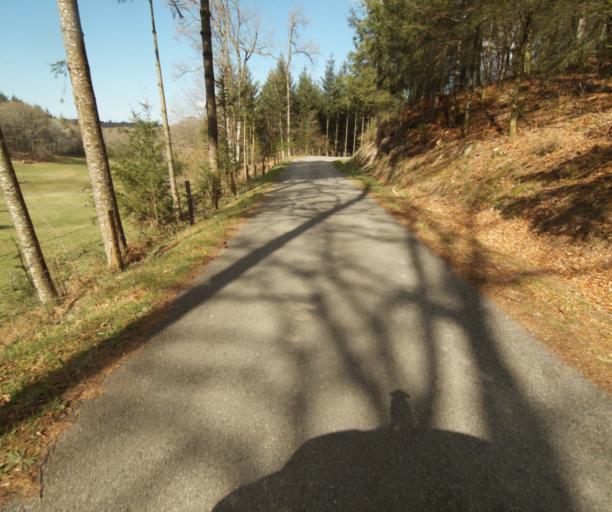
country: FR
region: Limousin
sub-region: Departement de la Correze
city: Argentat
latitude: 45.2305
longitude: 1.9225
